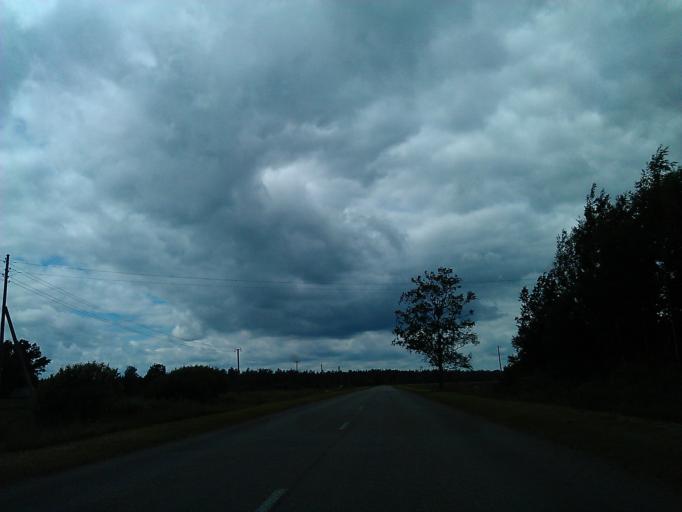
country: LV
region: Talsu Rajons
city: Stende
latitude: 57.0872
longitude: 22.3249
